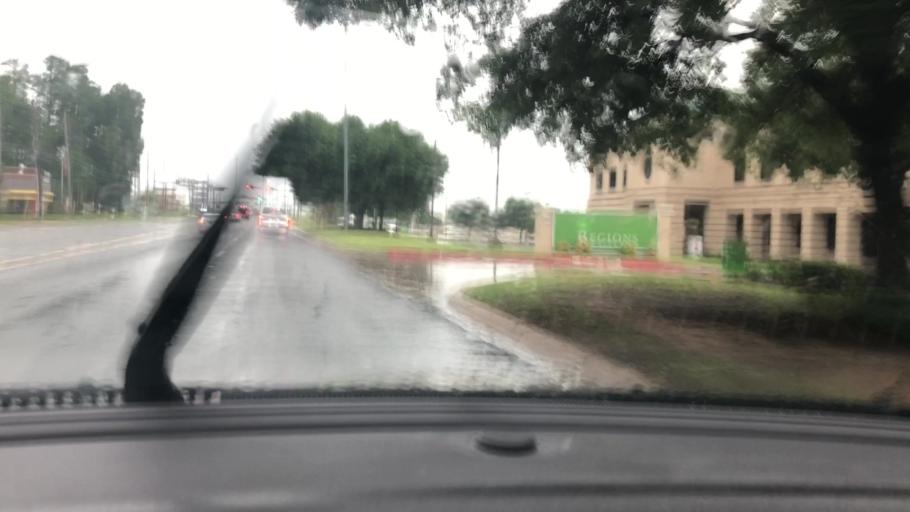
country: US
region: Texas
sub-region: Bowie County
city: Wake Village
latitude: 33.4527
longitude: -94.0812
